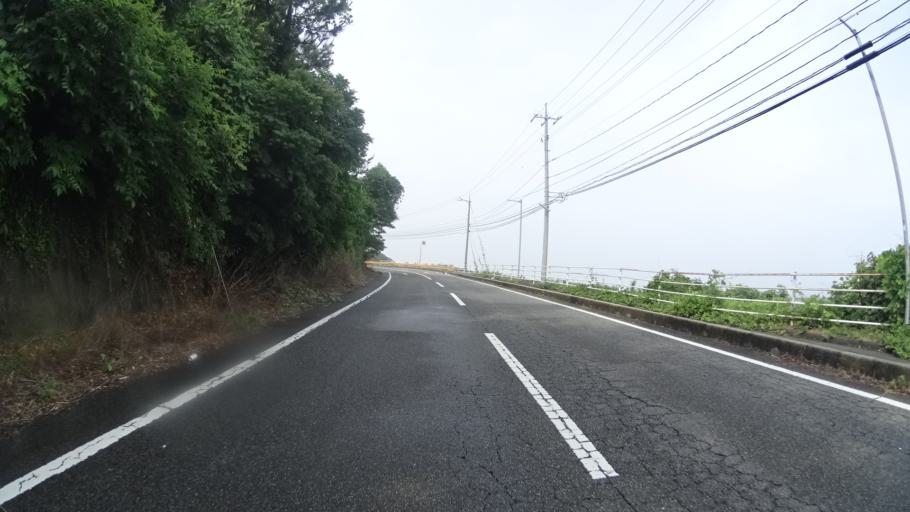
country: JP
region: Yamaguchi
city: Shimonoseki
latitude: 34.0860
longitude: 130.8816
